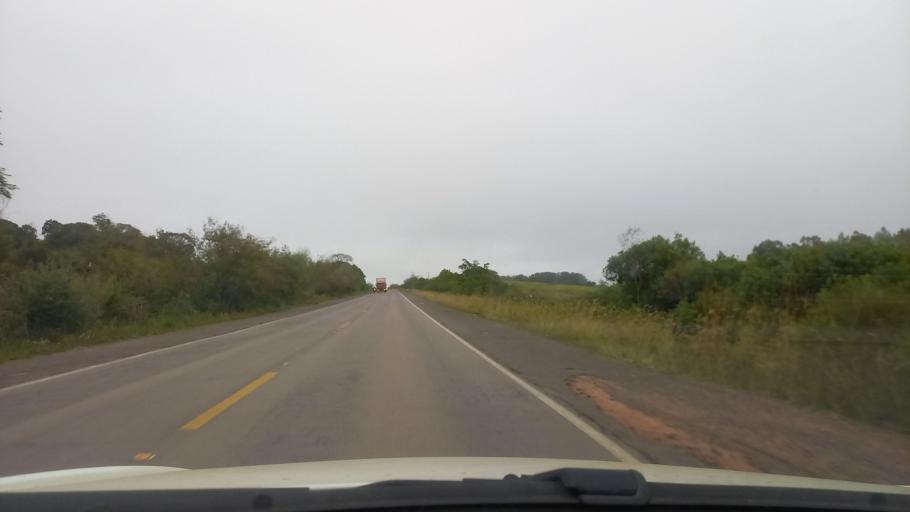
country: BR
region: Rio Grande do Sul
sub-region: Cacequi
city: Cacequi
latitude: -30.1234
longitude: -54.6463
